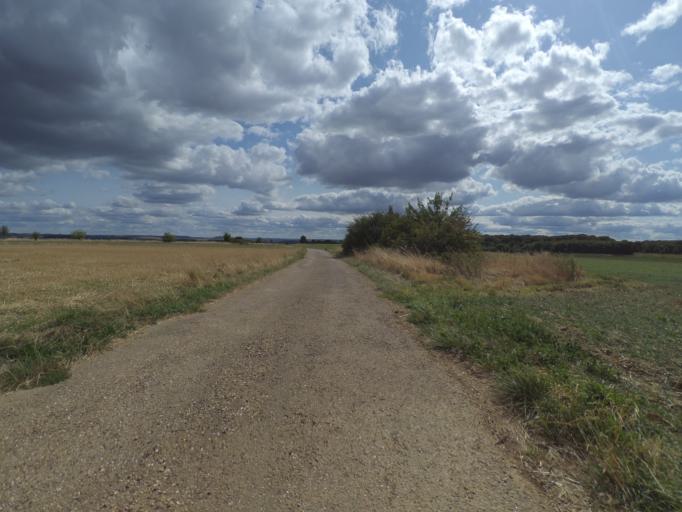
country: LU
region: Grevenmacher
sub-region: Canton de Remich
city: Mondorf-les-Bains
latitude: 49.5262
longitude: 6.2865
